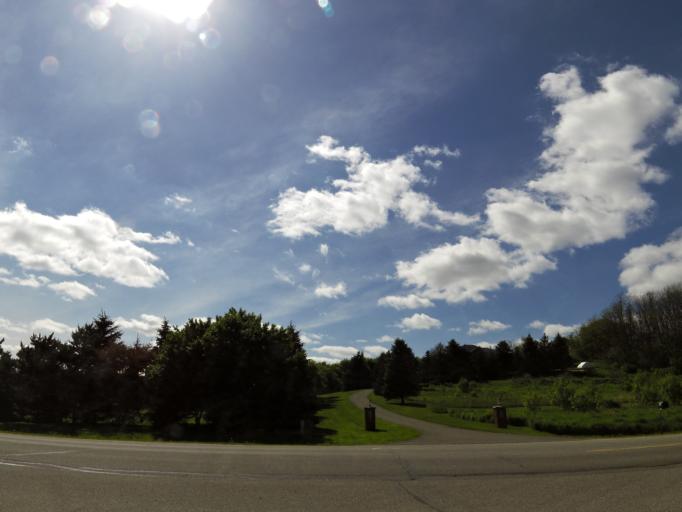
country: US
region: Wisconsin
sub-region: Saint Croix County
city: North Hudson
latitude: 44.9845
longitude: -92.7903
